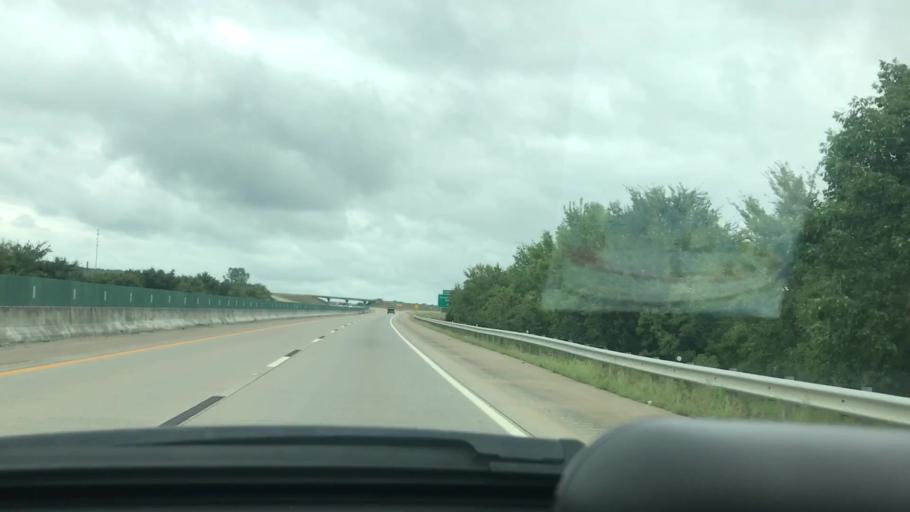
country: US
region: Oklahoma
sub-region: Pittsburg County
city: Krebs
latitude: 35.0517
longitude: -95.7088
